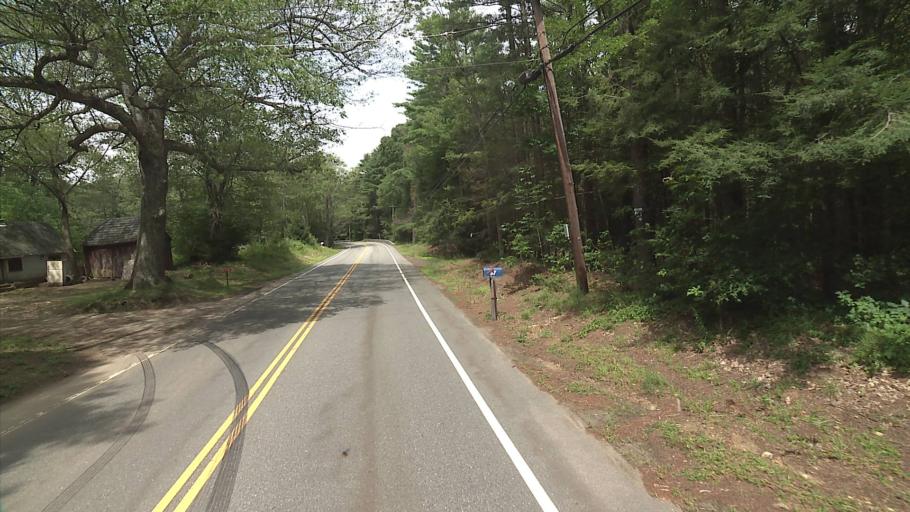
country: US
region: Massachusetts
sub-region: Hampden County
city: Holland
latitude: 41.9446
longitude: -72.1036
